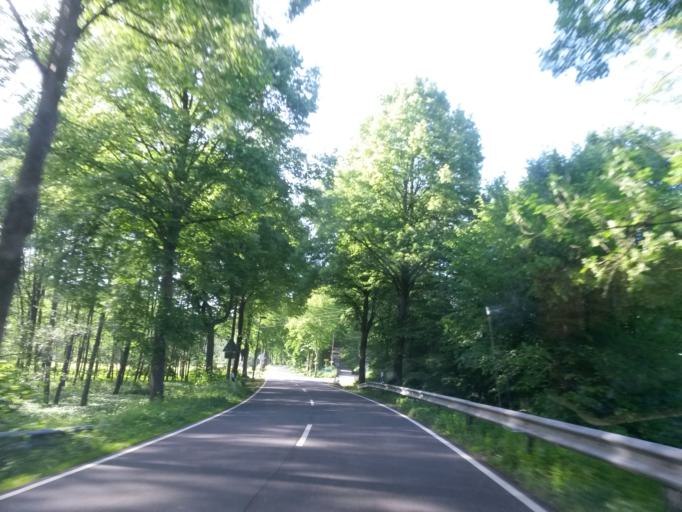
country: DE
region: North Rhine-Westphalia
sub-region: Regierungsbezirk Koln
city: Much
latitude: 50.8754
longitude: 7.3537
